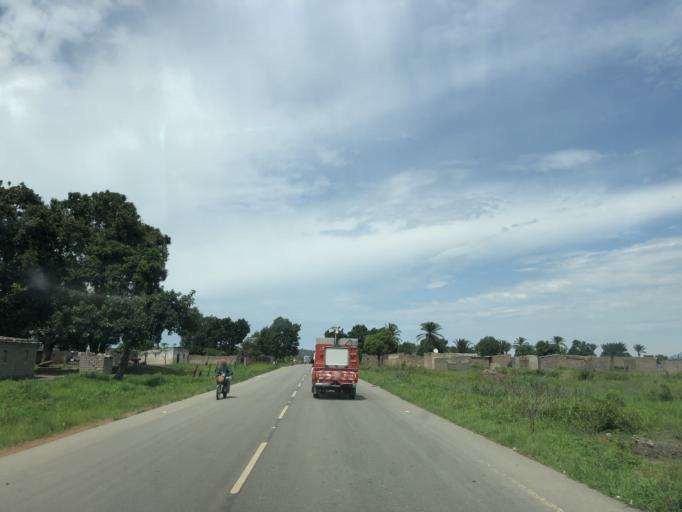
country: AO
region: Cuanza Sul
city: Quibala
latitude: -10.7355
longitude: 14.9966
